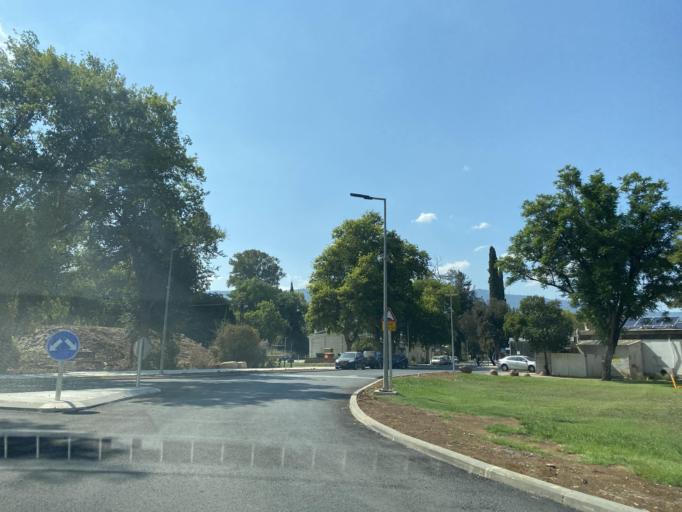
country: IL
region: Northern District
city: Qiryat Shemona
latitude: 33.1715
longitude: 35.6103
